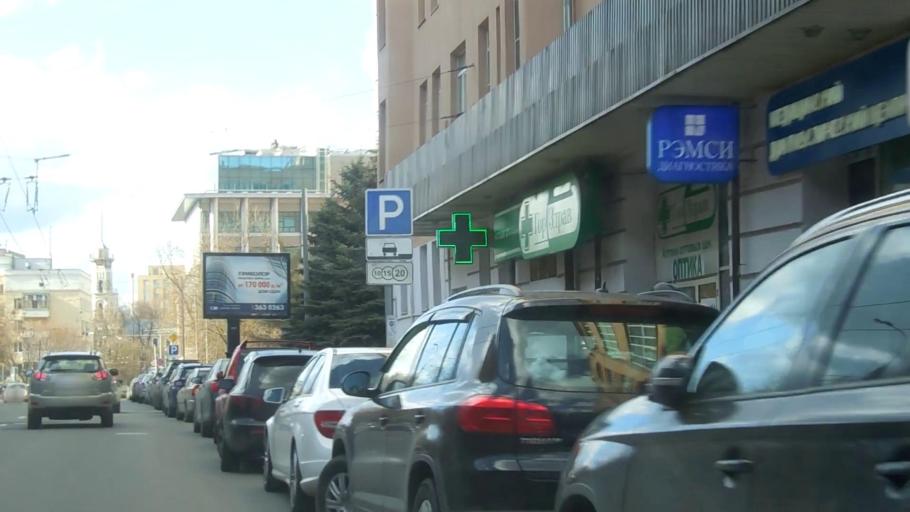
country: RU
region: Moscow
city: Mar'ina Roshcha
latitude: 55.7773
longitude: 37.6068
